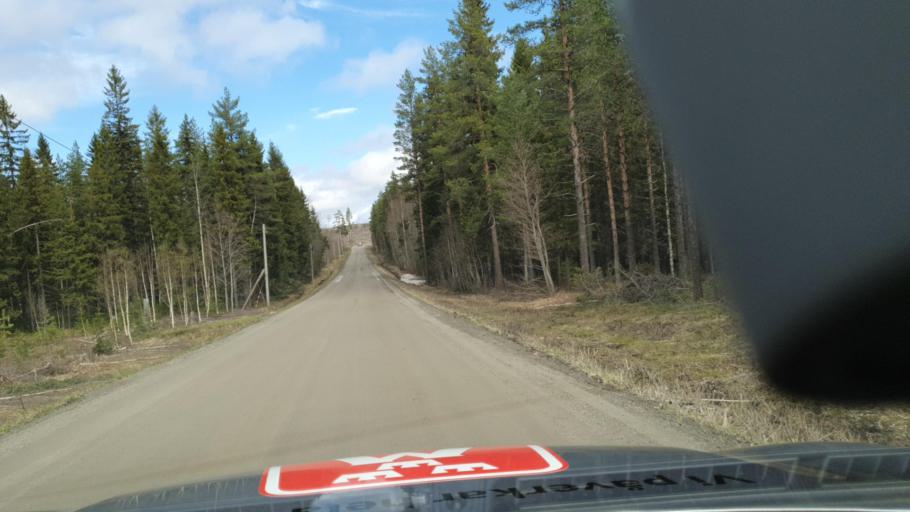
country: SE
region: Vaesterbotten
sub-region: Bjurholms Kommun
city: Bjurholm
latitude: 63.7019
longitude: 18.8997
